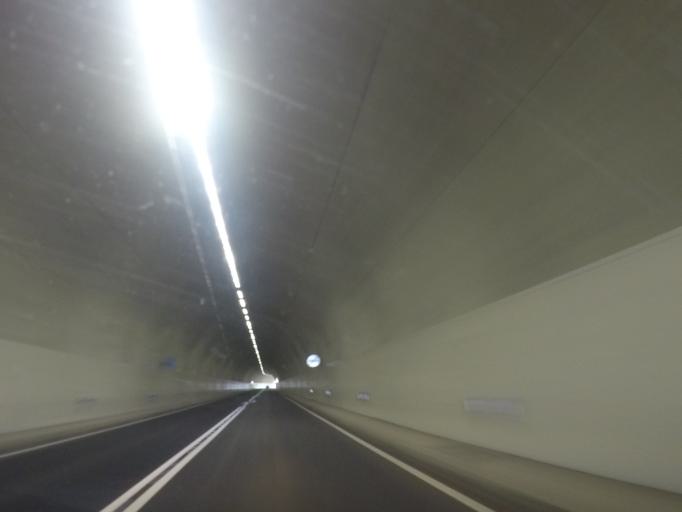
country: PT
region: Madeira
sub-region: Calheta
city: Faja da Ovelha
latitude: 32.7946
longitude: -17.2325
